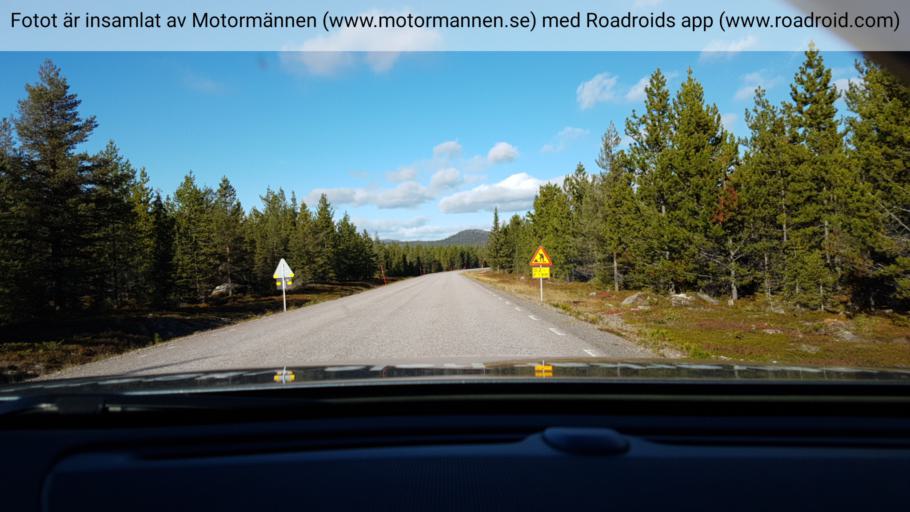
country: SE
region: Norrbotten
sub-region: Arjeplogs Kommun
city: Arjeplog
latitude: 65.8452
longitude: 18.4086
